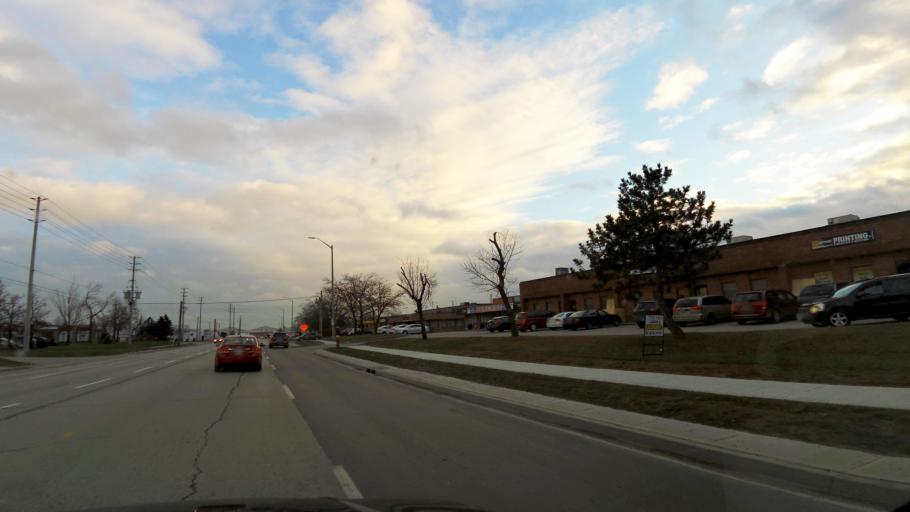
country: CA
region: Ontario
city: Etobicoke
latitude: 43.6972
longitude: -79.6568
